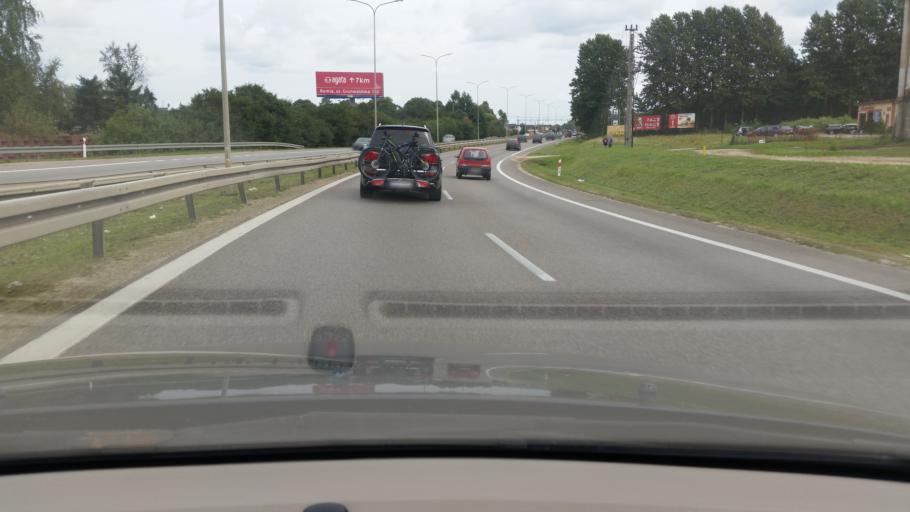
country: PL
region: Pomeranian Voivodeship
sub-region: Powiat wejherowski
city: Reda
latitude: 54.6049
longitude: 18.3108
